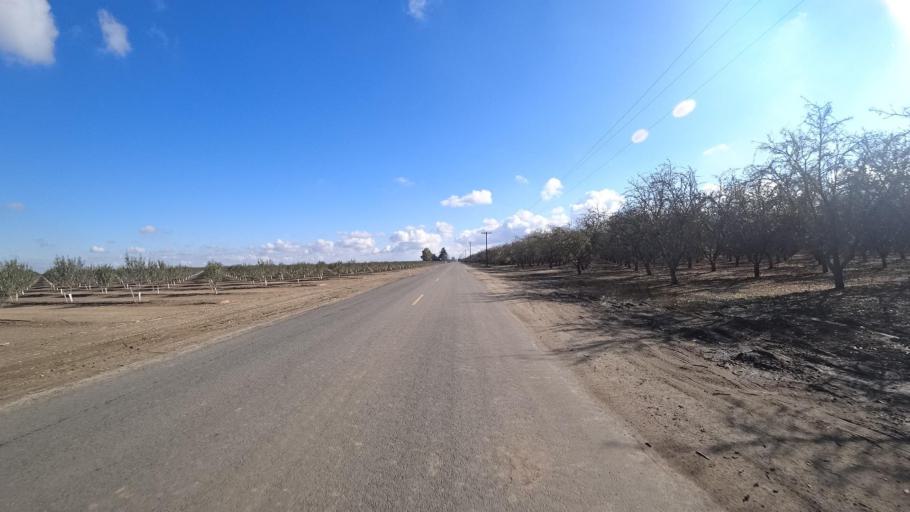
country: US
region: California
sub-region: Kern County
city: McFarland
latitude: 35.6598
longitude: -119.2564
